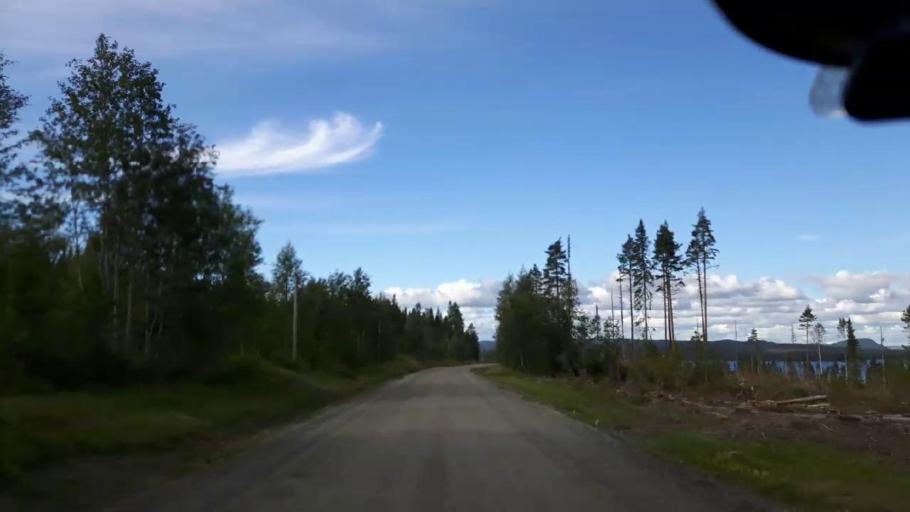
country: SE
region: Jaemtland
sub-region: Ragunda Kommun
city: Hammarstrand
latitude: 63.1348
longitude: 15.9477
